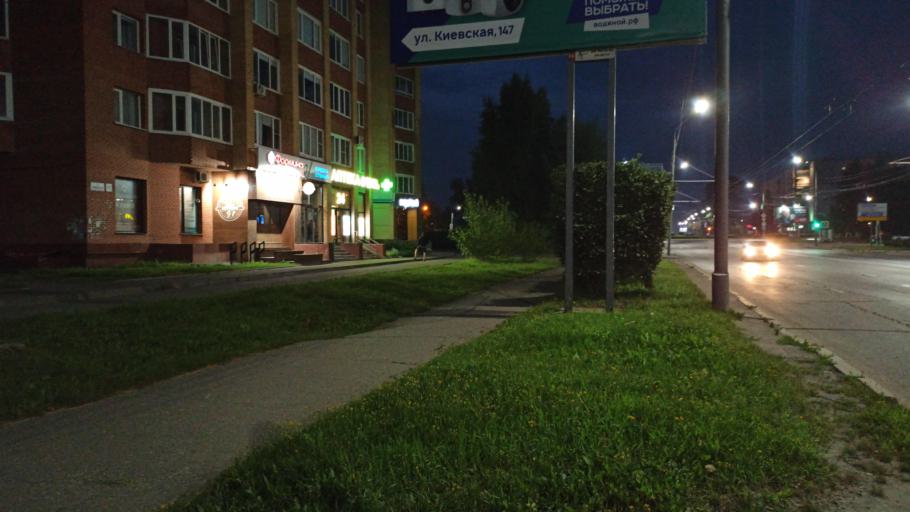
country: RU
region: Tomsk
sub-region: Tomskiy Rayon
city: Tomsk
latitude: 56.4570
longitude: 84.9736
